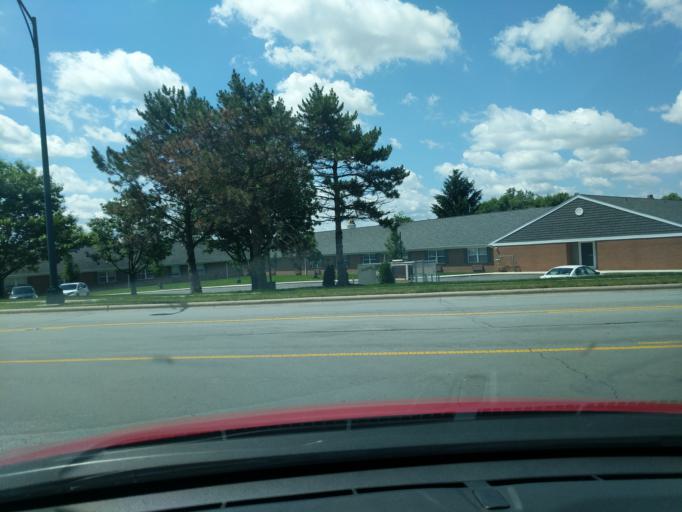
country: US
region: Ohio
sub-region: Franklin County
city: Gahanna
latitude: 40.0621
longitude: -82.8643
